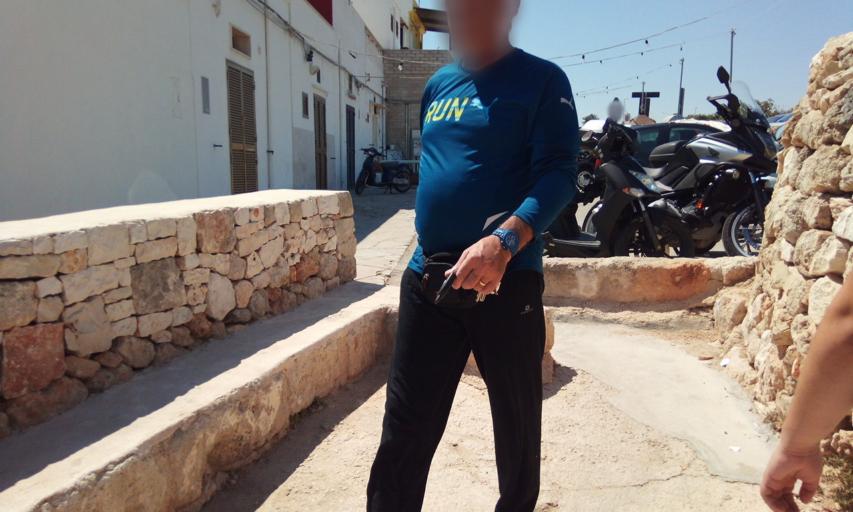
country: IT
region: Apulia
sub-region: Provincia di Bari
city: Polignano a Mare
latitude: 40.9906
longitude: 17.2378
